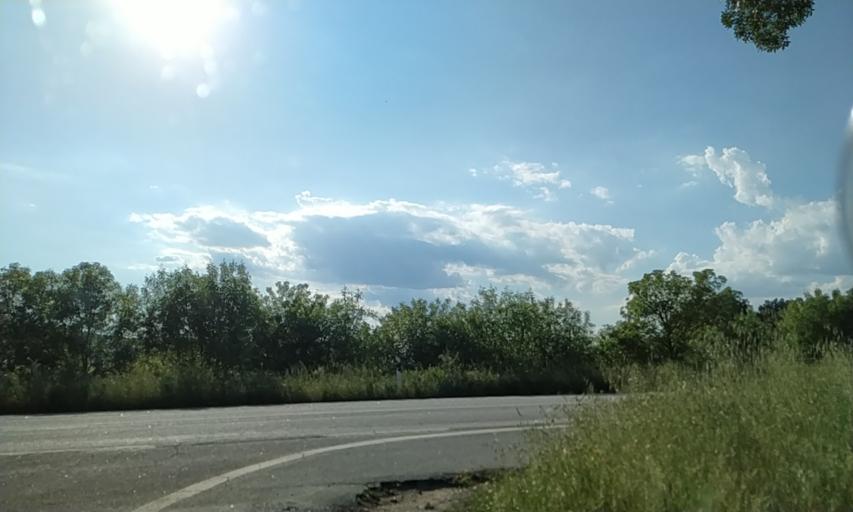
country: PT
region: Portalegre
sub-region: Portalegre
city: Urra
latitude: 39.0951
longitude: -7.4371
